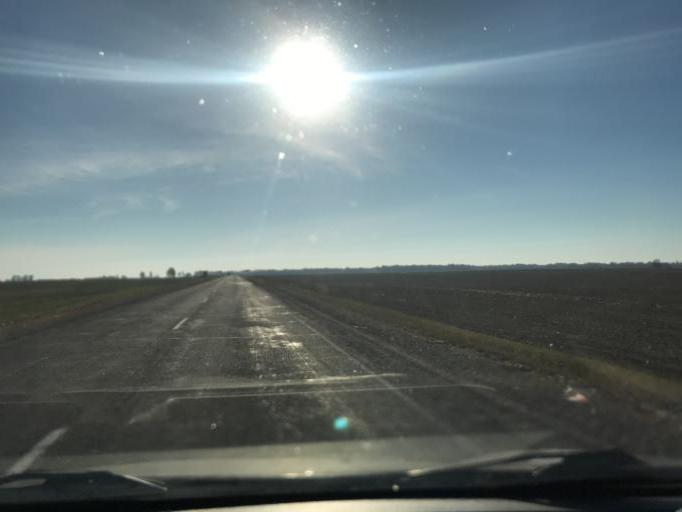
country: BY
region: Gomel
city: Brahin
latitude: 51.8079
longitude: 30.1105
